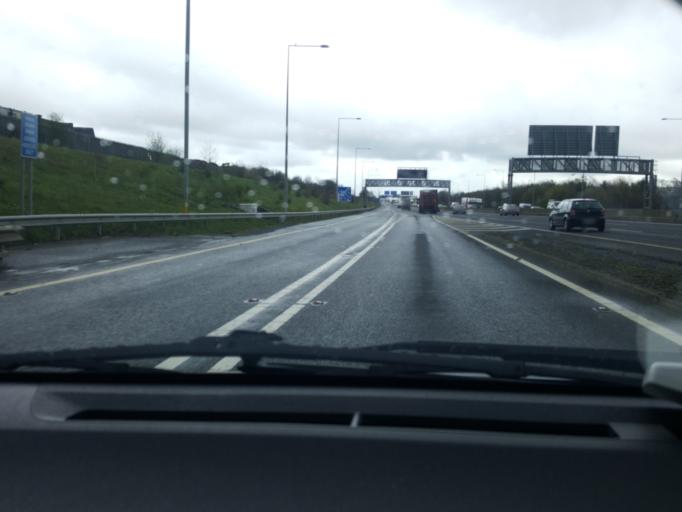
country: IE
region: Leinster
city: Ballymun
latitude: 53.4096
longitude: -6.2607
